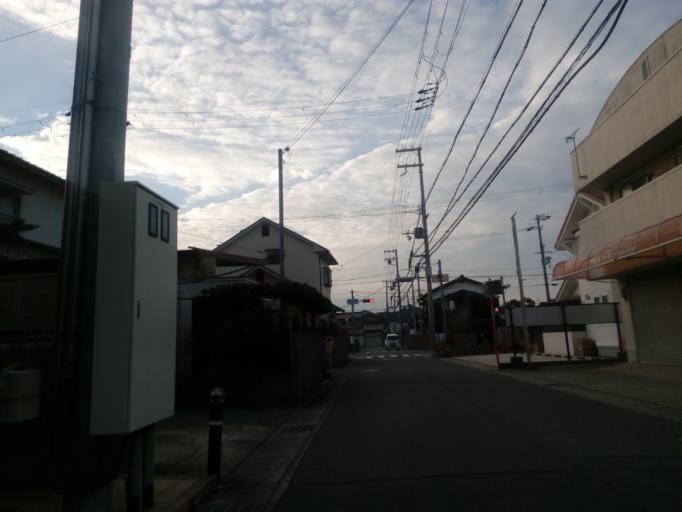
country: JP
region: Hyogo
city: Himeji
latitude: 34.8134
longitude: 134.6734
